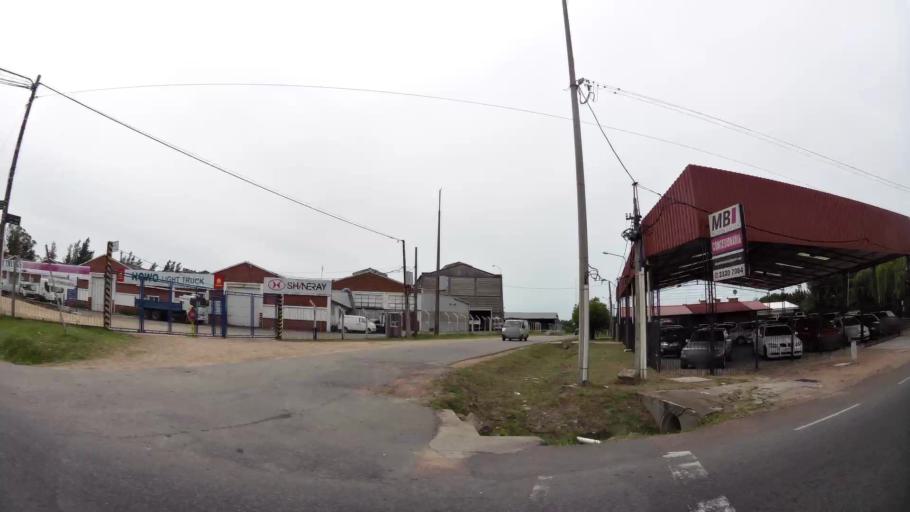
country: UY
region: Canelones
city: La Paz
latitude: -34.7896
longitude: -56.2242
